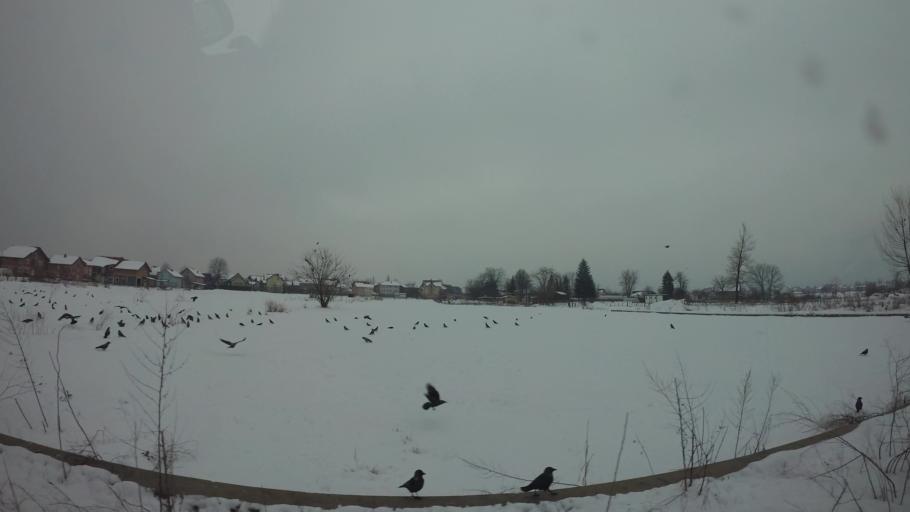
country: BA
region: Federation of Bosnia and Herzegovina
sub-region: Kanton Sarajevo
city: Sarajevo
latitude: 43.8446
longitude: 18.2874
